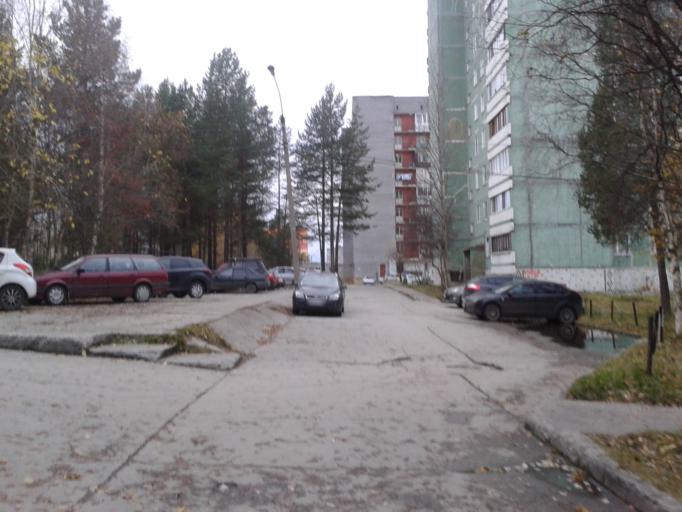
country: RU
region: Murmansk
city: Polyarnyye Zori
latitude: 67.3721
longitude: 32.4981
